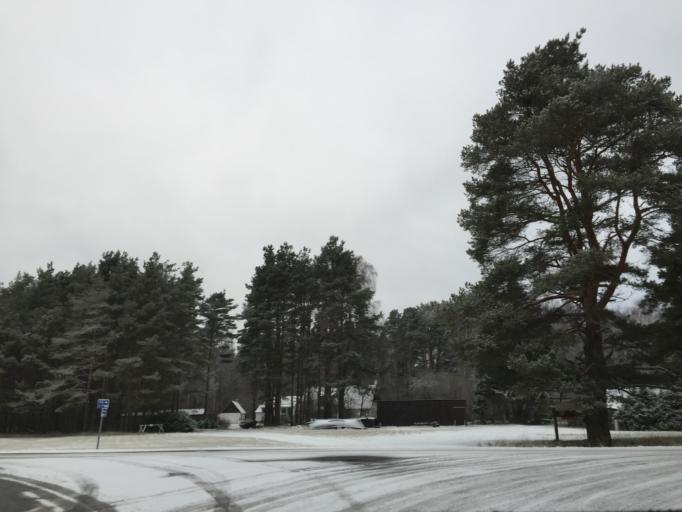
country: EE
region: Saare
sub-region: Orissaare vald
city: Orissaare
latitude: 58.6120
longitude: 23.2977
